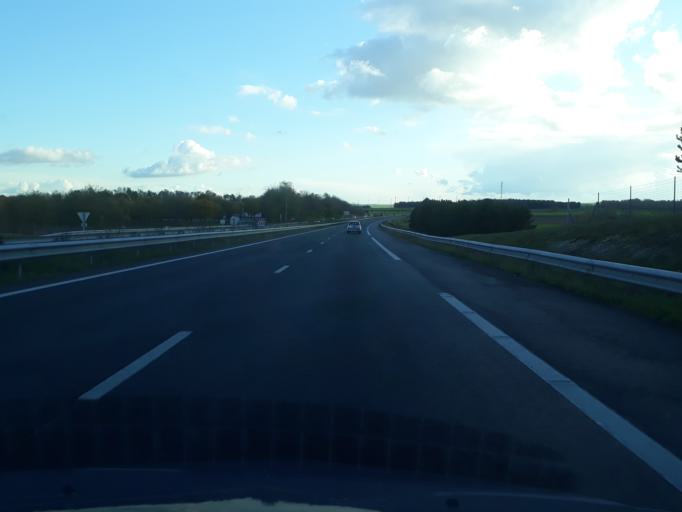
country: FR
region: Champagne-Ardenne
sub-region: Departement de la Marne
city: Compertrix
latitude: 48.8894
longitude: 4.2890
